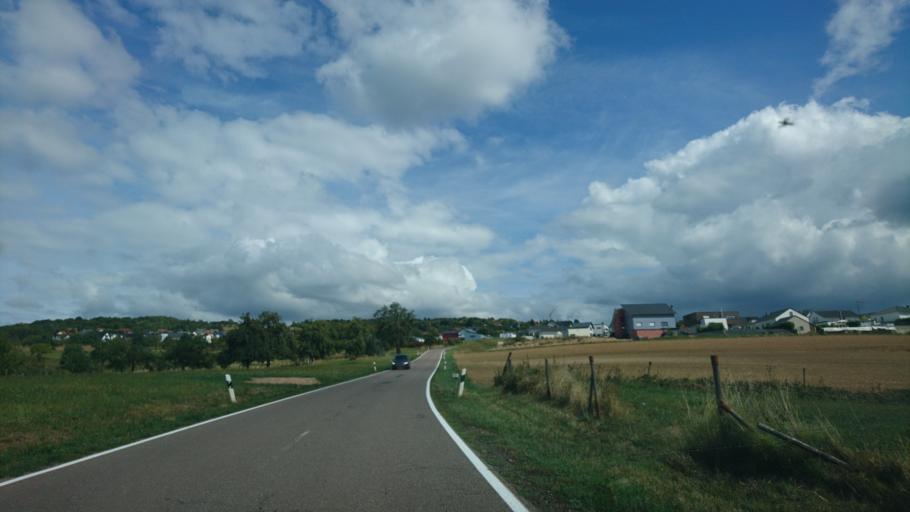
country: DE
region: Rheinland-Pfalz
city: Freudenburg
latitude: 49.5441
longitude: 6.5211
